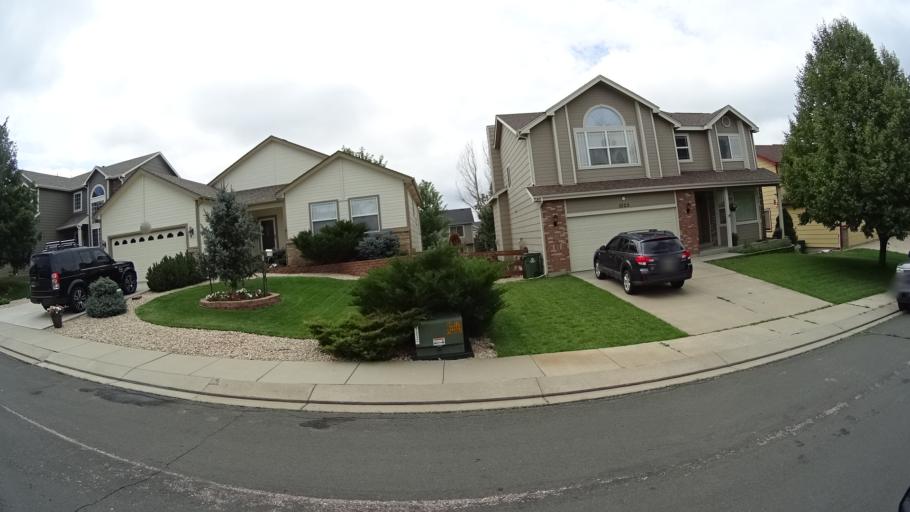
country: US
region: Colorado
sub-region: El Paso County
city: Gleneagle
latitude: 39.0094
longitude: -104.8018
